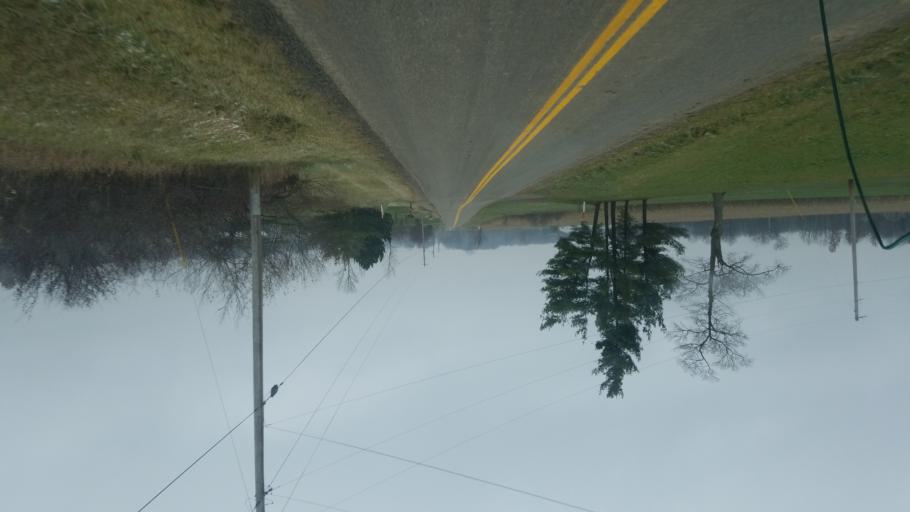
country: US
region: Ohio
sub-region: Huron County
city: New London
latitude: 41.0088
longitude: -82.3548
